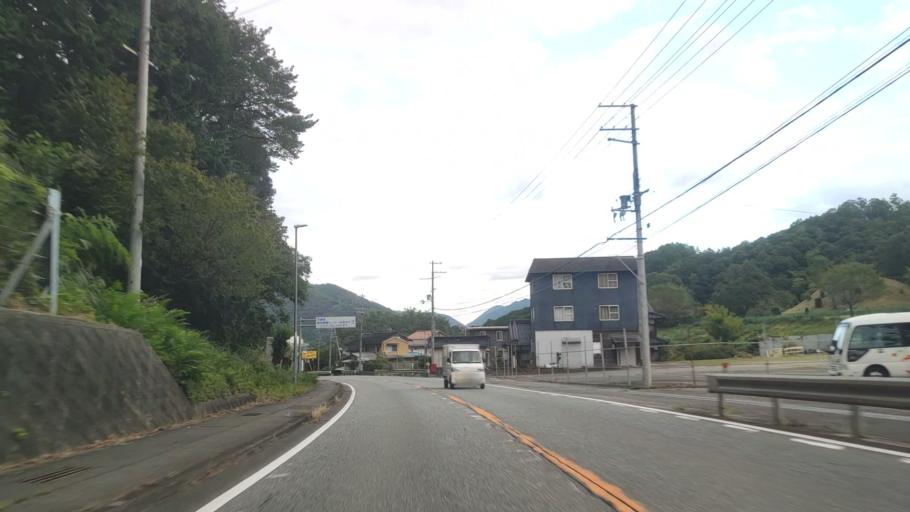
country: JP
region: Hyogo
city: Toyooka
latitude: 35.3673
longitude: 134.8044
